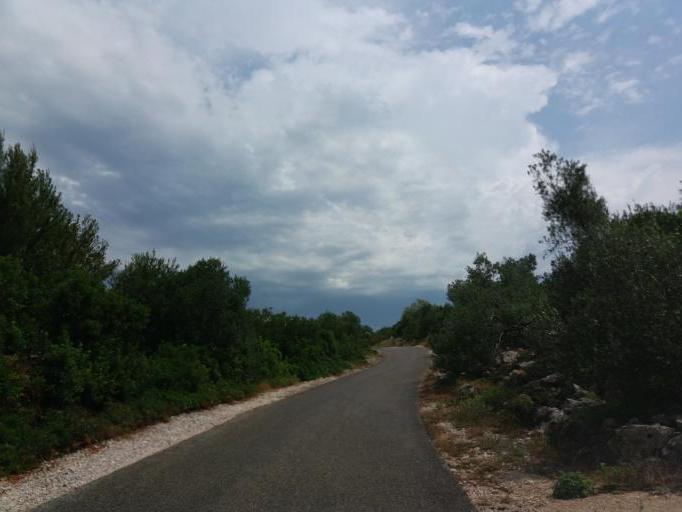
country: HR
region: Zadarska
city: Sali
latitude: 43.9337
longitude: 15.1391
